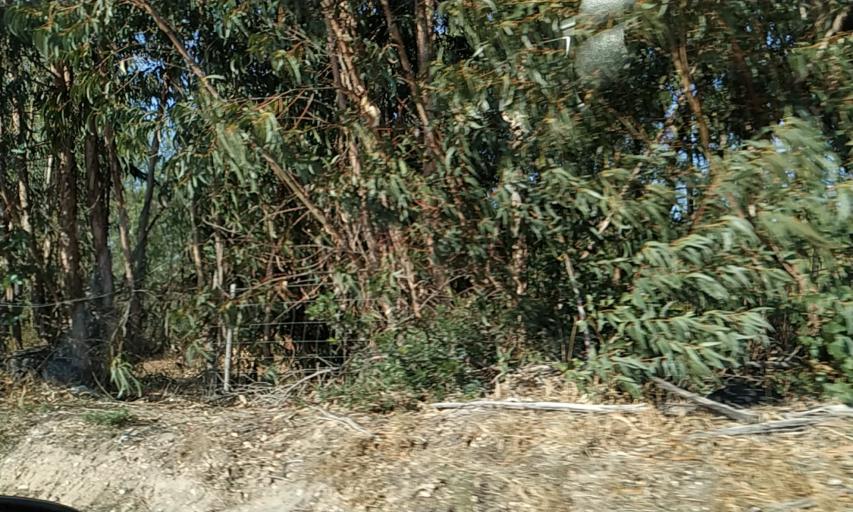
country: PT
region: Santarem
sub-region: Almeirim
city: Fazendas de Almeirim
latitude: 39.1251
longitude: -8.6031
